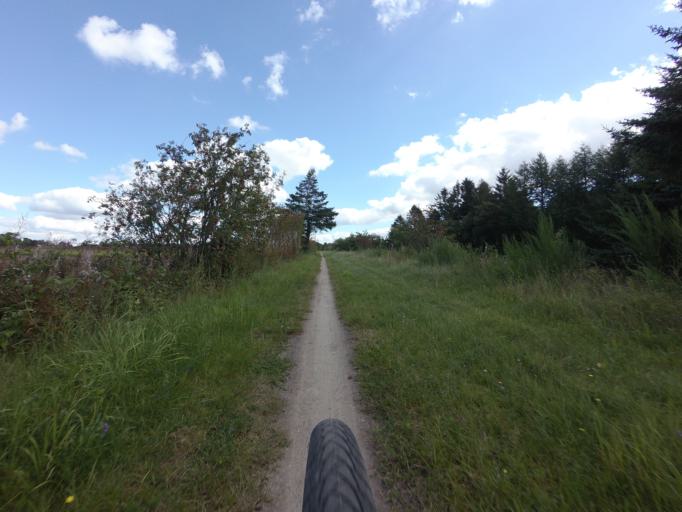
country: DK
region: South Denmark
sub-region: Vejle Kommune
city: Give
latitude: 55.9799
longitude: 9.2667
